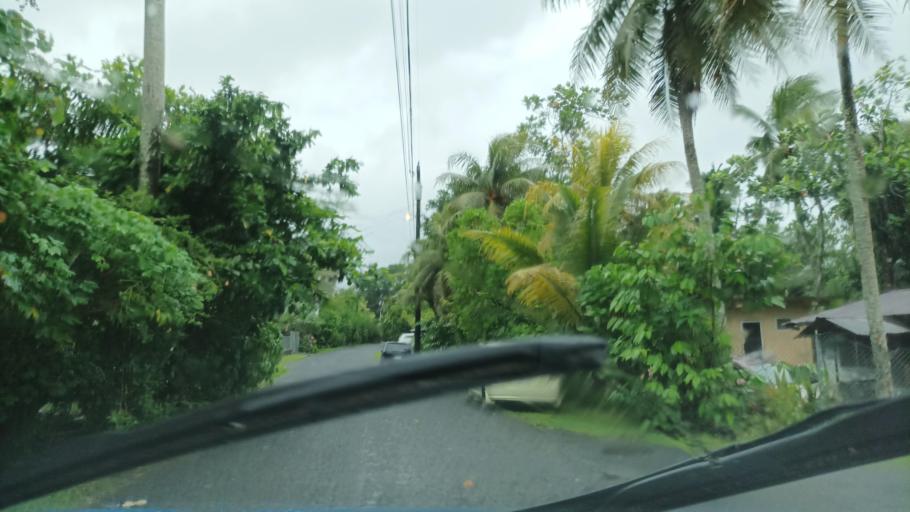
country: FM
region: Pohnpei
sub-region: Kolonia Municipality
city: Kolonia
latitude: 6.9700
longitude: 158.2075
